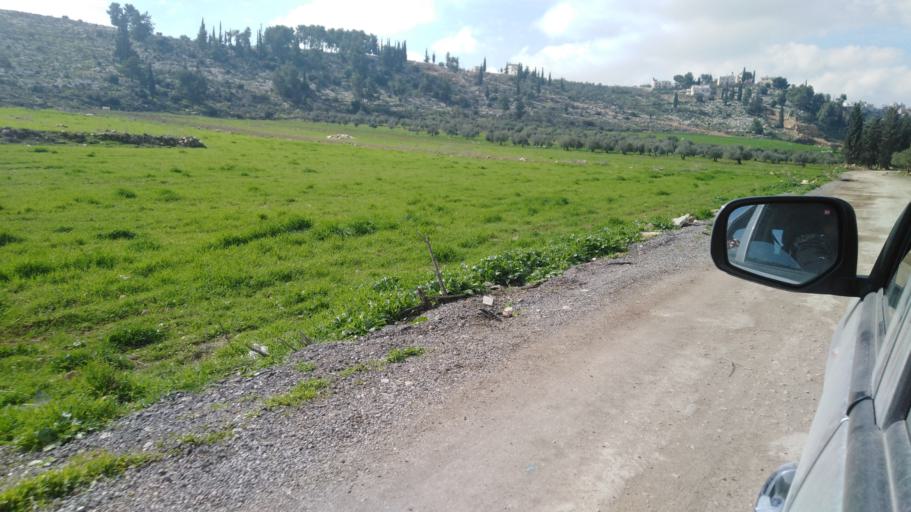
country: PS
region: West Bank
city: Idhna
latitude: 31.5565
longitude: 34.9957
